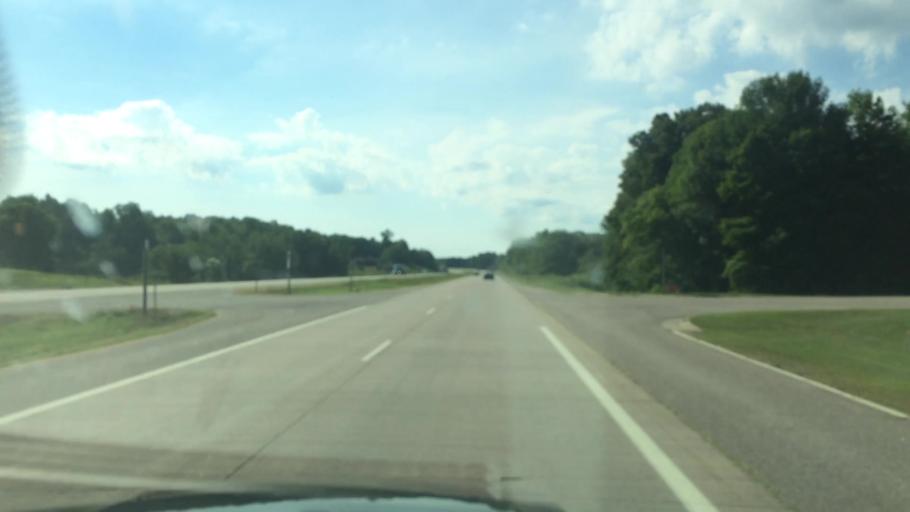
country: US
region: Wisconsin
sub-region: Shawano County
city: Wittenberg
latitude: 44.8106
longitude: -89.0417
